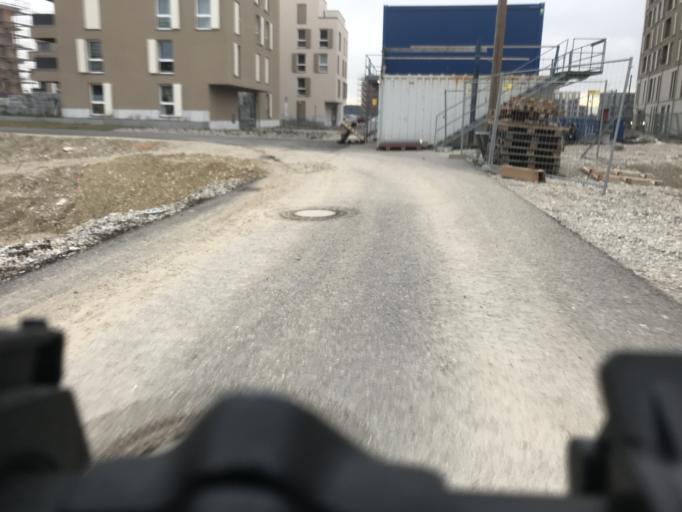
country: DE
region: Bavaria
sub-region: Upper Bavaria
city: Germering
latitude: 48.1491
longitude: 11.4069
